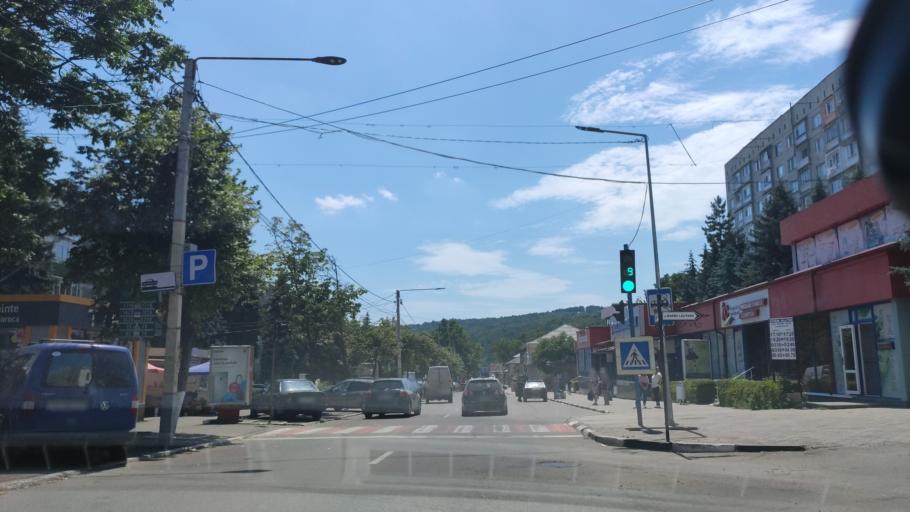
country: MD
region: Raionul Soroca
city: Soroca
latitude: 48.1607
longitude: 28.3008
